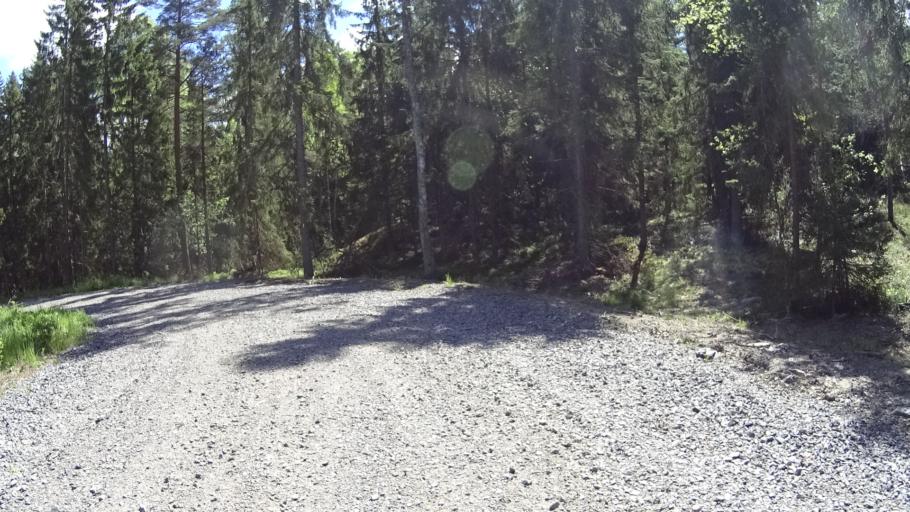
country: FI
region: Uusimaa
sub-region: Helsinki
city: Espoo
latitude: 60.2074
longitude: 24.6200
